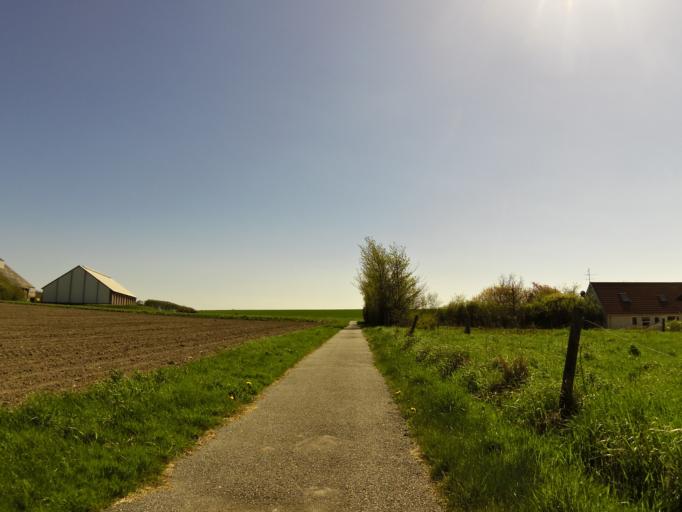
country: DK
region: Central Jutland
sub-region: Holstebro Kommune
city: Vinderup
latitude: 56.5996
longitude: 8.7738
